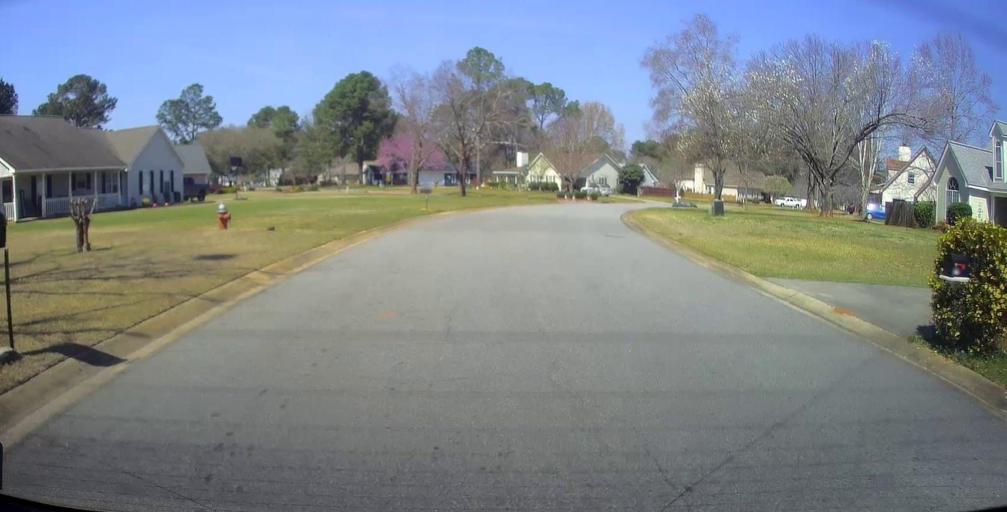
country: US
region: Georgia
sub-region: Houston County
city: Centerville
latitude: 32.5886
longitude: -83.7097
